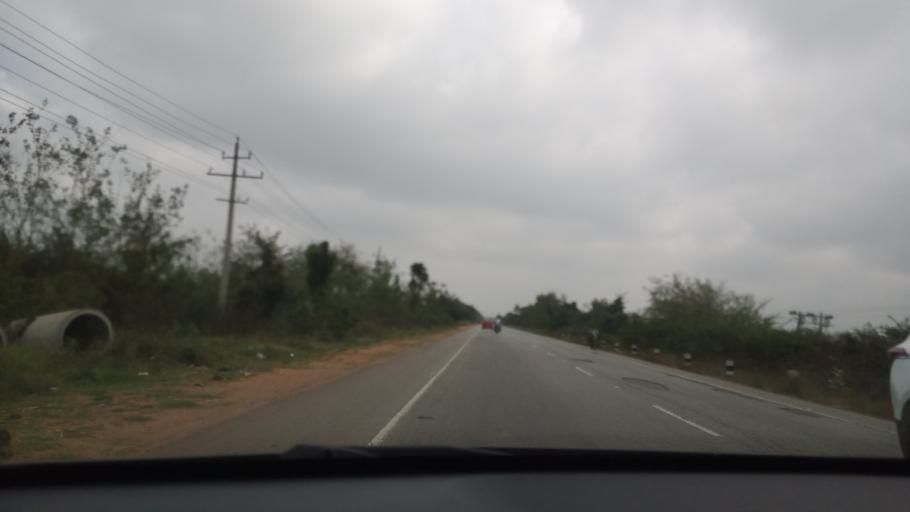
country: IN
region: Karnataka
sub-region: Chikkaballapur
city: Chintamani
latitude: 13.3403
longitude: 78.0097
